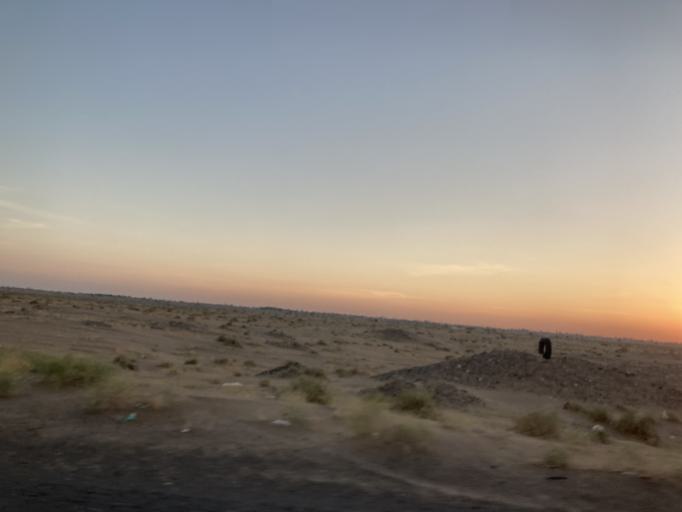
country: YE
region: Lahij
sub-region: Al  Hawtah
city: Lahij
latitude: 13.1045
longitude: 44.9007
